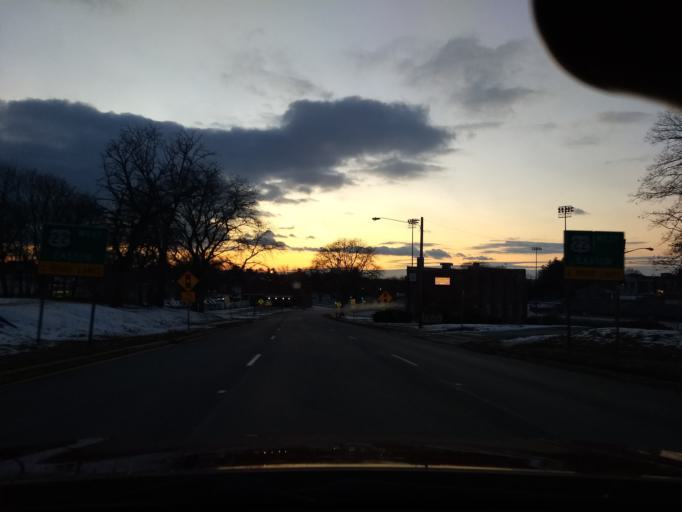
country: US
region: New Jersey
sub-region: Warren County
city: Phillipsburg
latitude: 40.6967
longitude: -75.1877
